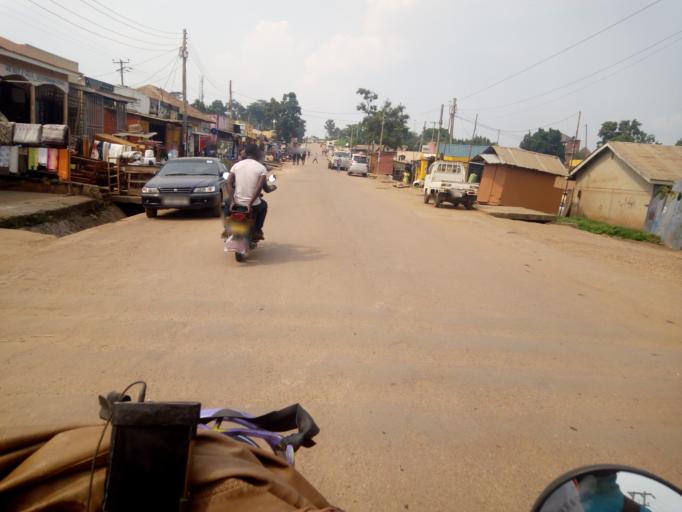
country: UG
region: Central Region
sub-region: Wakiso District
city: Kireka
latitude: 0.3060
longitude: 32.6531
